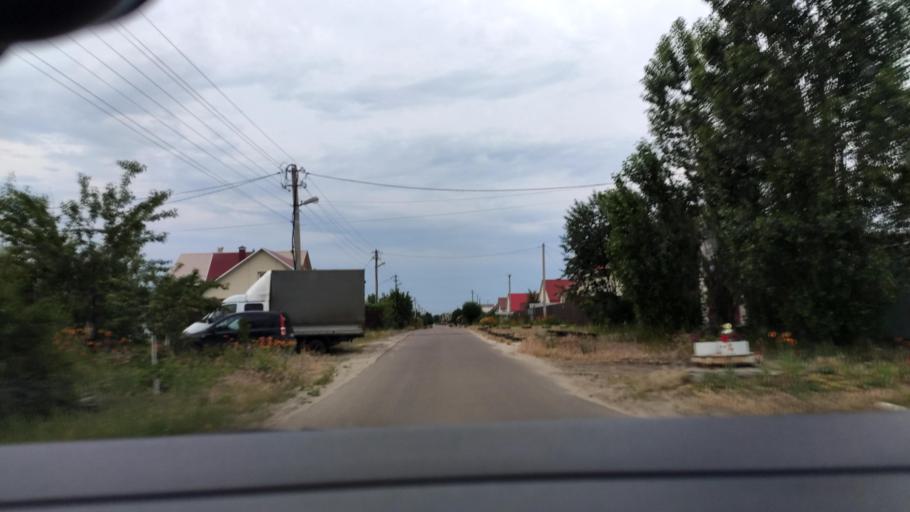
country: RU
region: Voronezj
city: Maslovka
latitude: 51.5688
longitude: 39.2502
